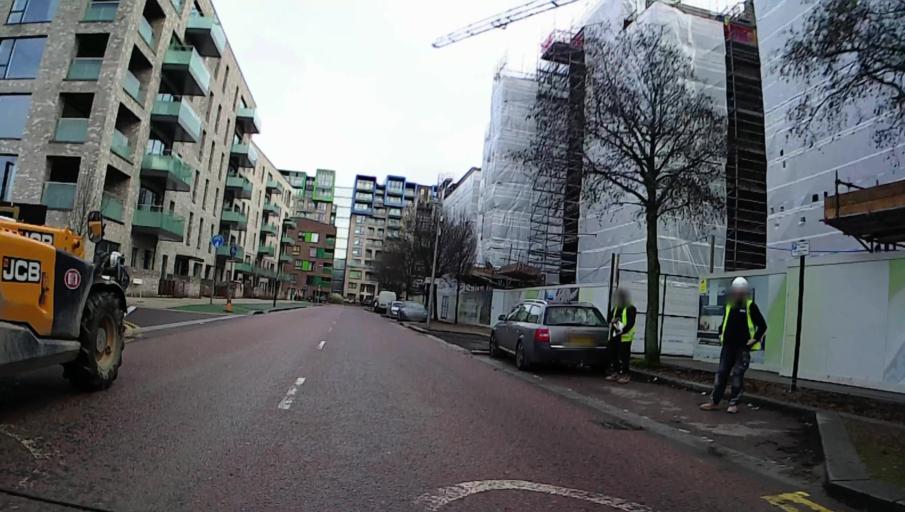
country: GB
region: England
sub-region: Greater London
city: Blackheath
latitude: 51.4925
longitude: 0.0166
